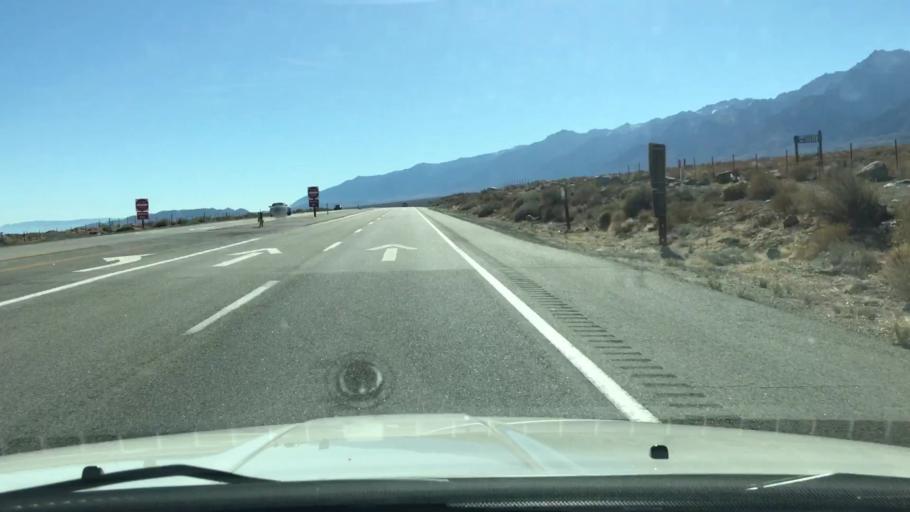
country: US
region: California
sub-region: Inyo County
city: Lone Pine
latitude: 36.8478
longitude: -118.2318
